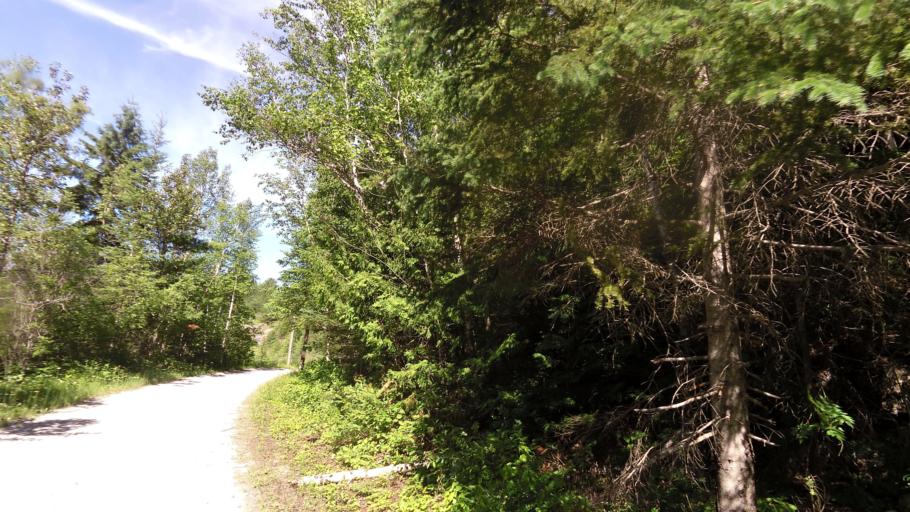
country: CA
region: Ontario
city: Temiskaming Shores
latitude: 47.3868
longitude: -79.6870
